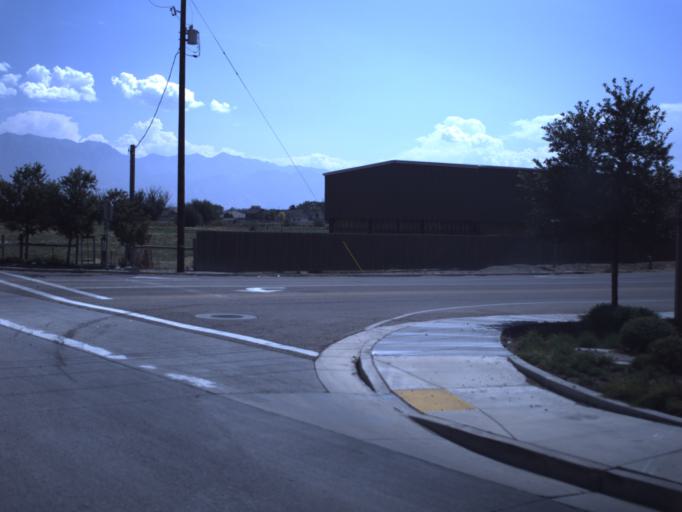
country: US
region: Utah
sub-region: Utah County
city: Lehi
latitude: 40.3734
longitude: -111.8447
